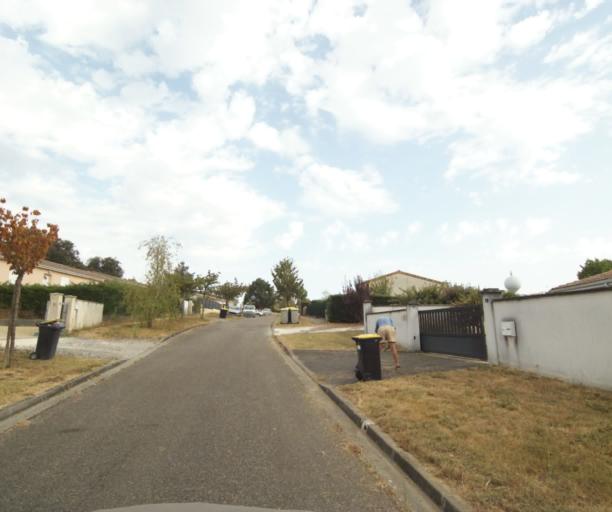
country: FR
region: Aquitaine
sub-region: Departement de la Gironde
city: Creon
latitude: 44.7678
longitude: -0.3462
